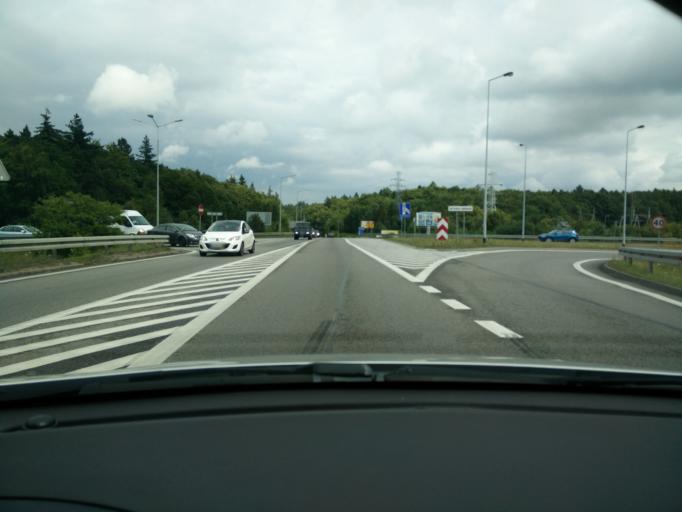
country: PL
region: Pomeranian Voivodeship
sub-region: Gdynia
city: Wielki Kack
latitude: 54.4294
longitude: 18.4893
